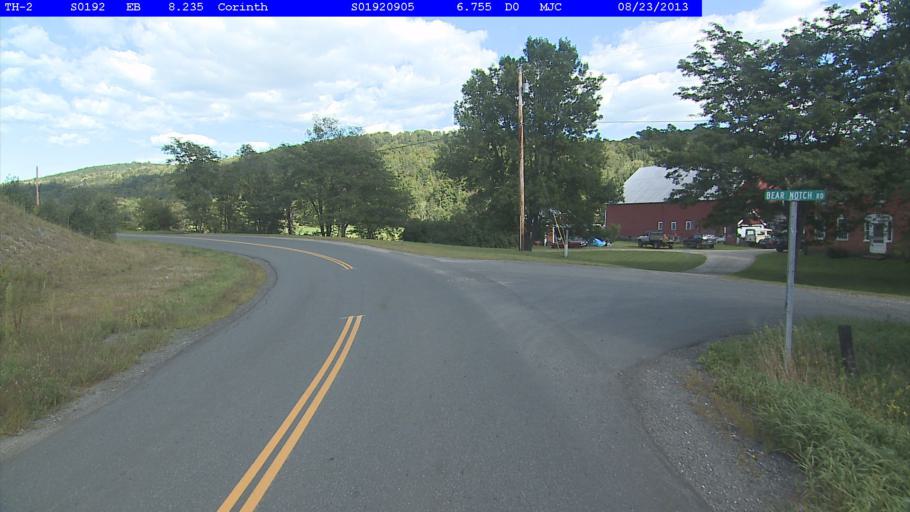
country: US
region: New Hampshire
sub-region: Grafton County
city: Orford
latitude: 44.0085
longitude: -72.2423
